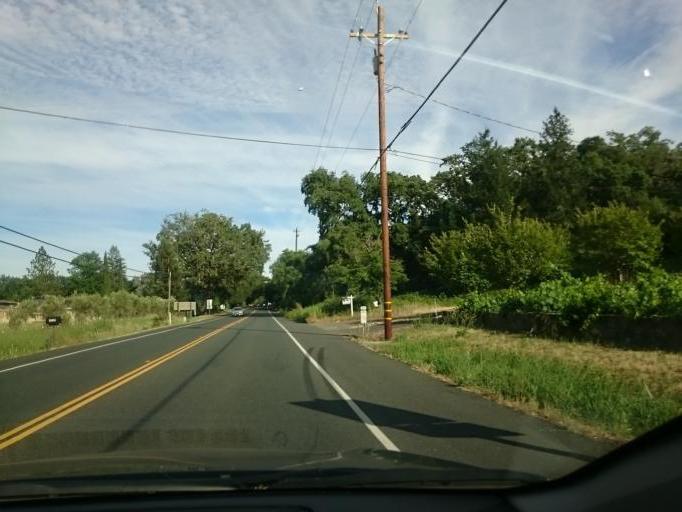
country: US
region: California
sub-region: Napa County
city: Calistoga
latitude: 38.5855
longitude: -122.6035
